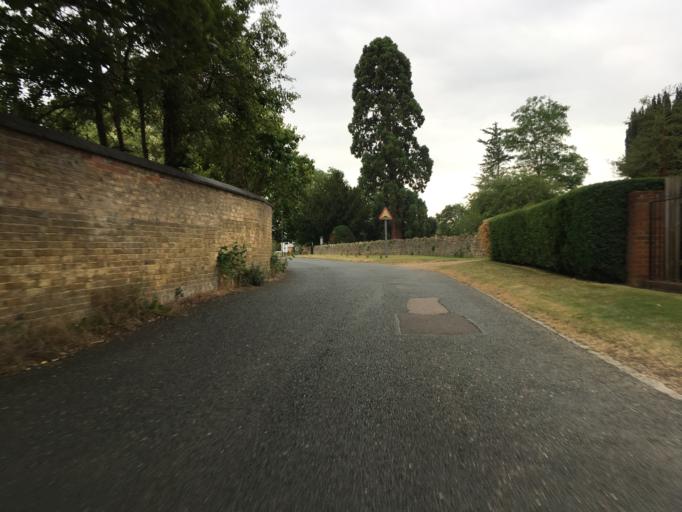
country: GB
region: England
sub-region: Milton Keynes
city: Broughton
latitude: 52.0443
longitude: -0.7065
